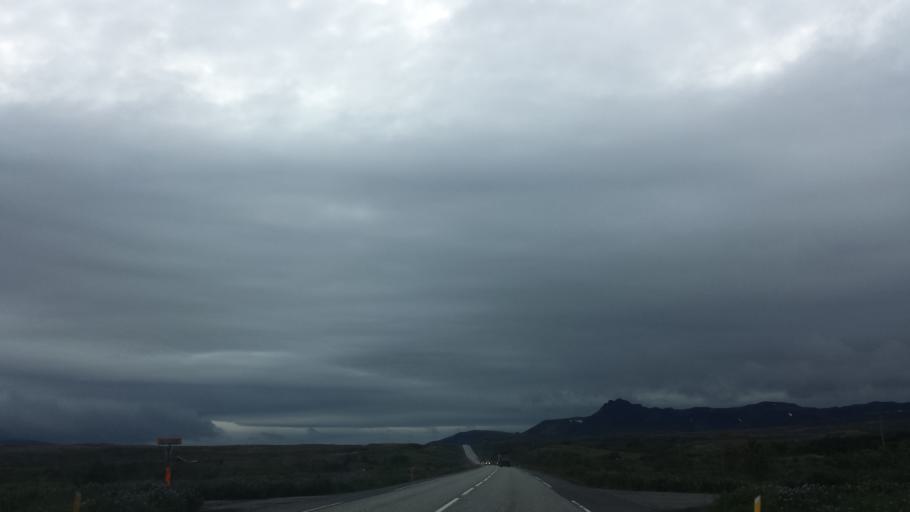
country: IS
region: Capital Region
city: Mosfellsbaer
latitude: 64.0827
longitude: -21.6751
